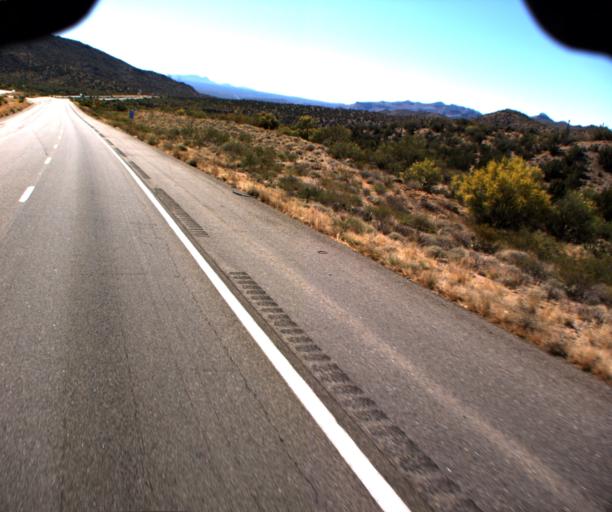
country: US
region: Arizona
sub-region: Yavapai County
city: Bagdad
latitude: 34.4292
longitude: -113.2493
